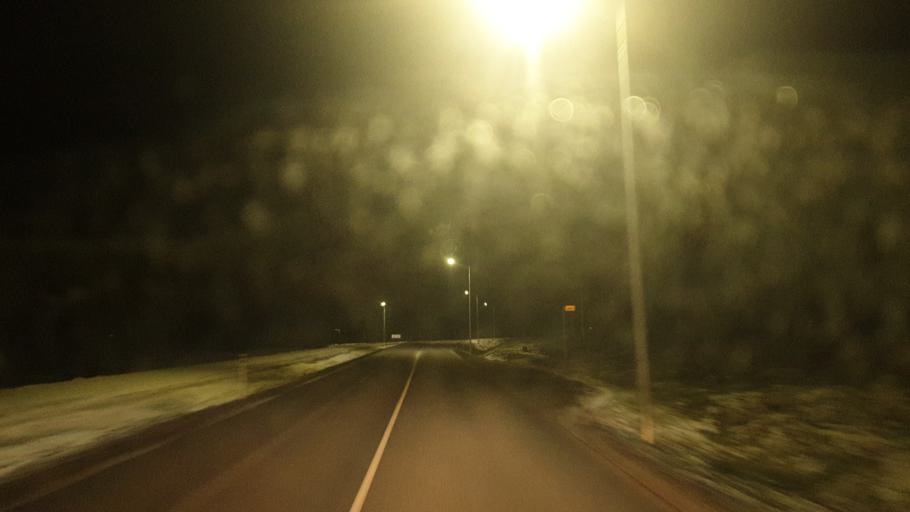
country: FI
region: Southern Savonia
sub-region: Pieksaemaeki
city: Juva
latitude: 61.8767
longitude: 27.7724
